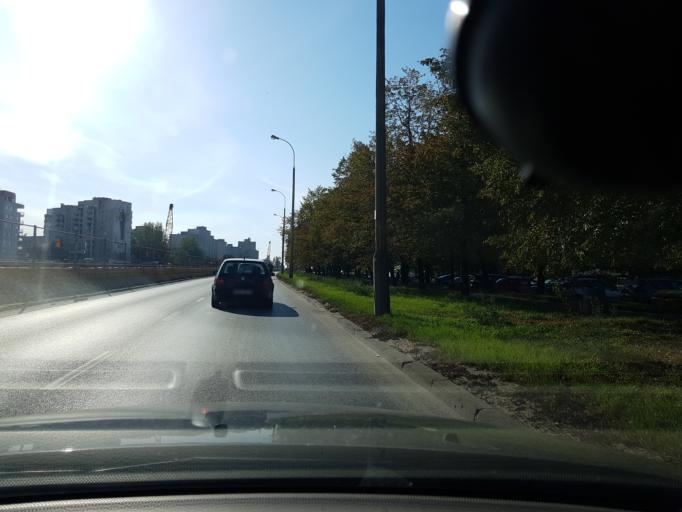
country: PL
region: Masovian Voivodeship
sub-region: Warszawa
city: Ursynow
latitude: 52.1435
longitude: 21.0478
